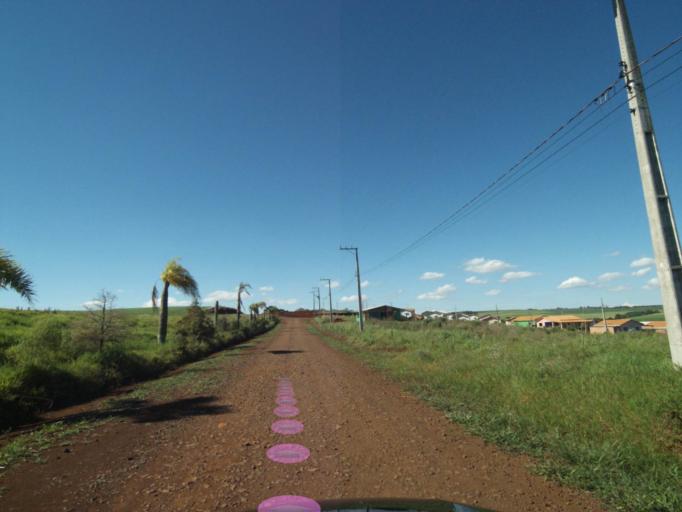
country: BR
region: Parana
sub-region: Coronel Vivida
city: Coronel Vivida
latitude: -26.1383
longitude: -52.3935
